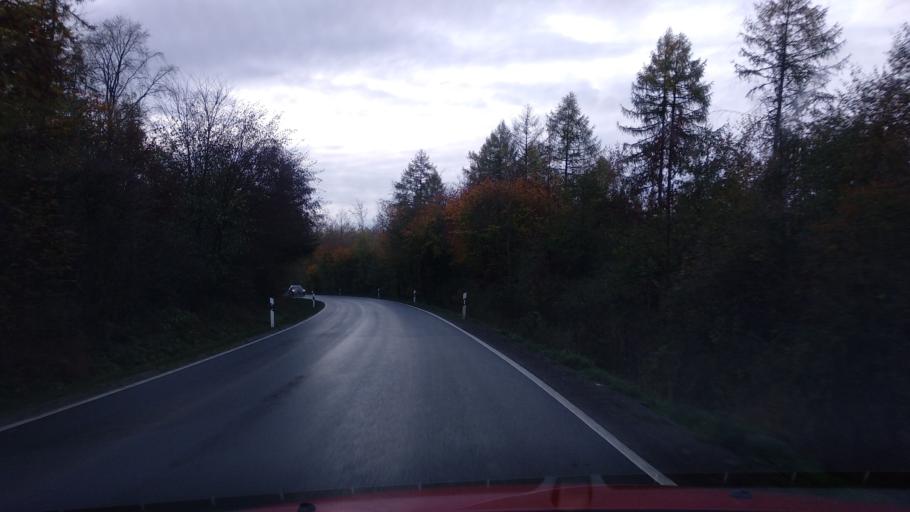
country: DE
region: North Rhine-Westphalia
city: Brakel
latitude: 51.6687
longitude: 9.2565
